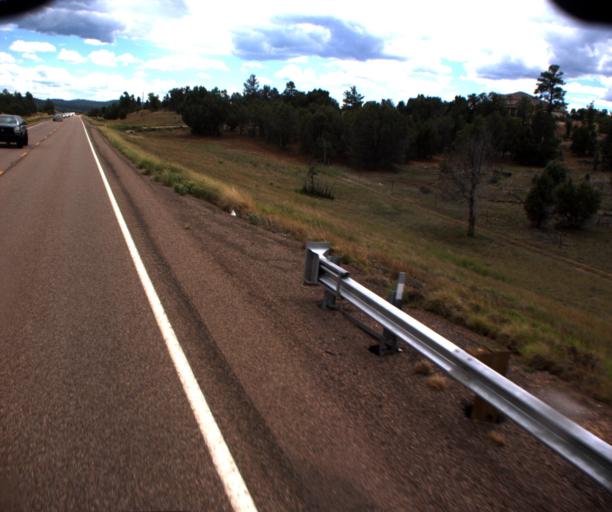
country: US
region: Arizona
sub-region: Navajo County
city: Linden
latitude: 34.3245
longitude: -110.2565
